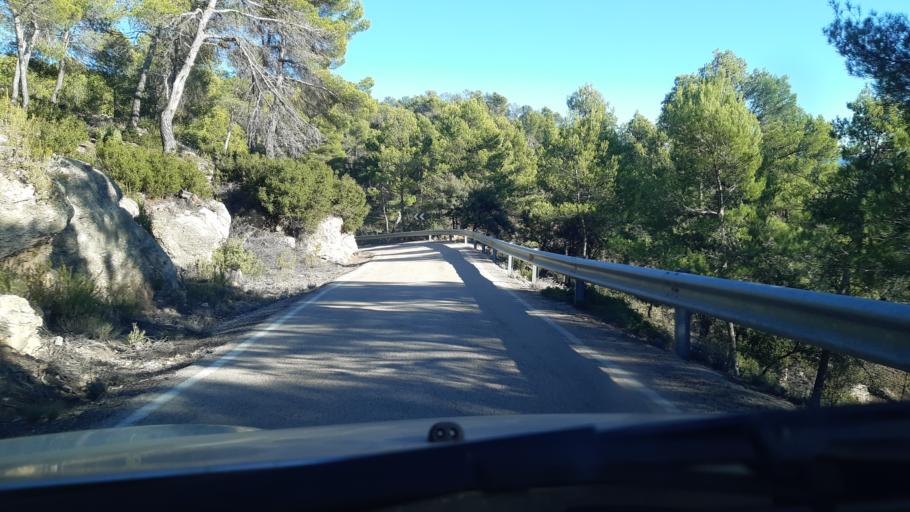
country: ES
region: Aragon
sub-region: Provincia de Teruel
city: Fornoles
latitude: 40.9102
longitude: -0.0160
